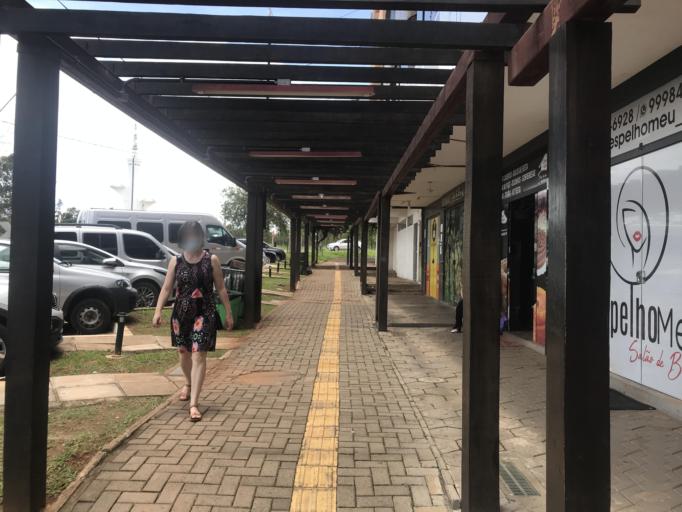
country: BR
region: Federal District
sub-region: Brasilia
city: Brasilia
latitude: -15.6923
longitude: -47.8262
